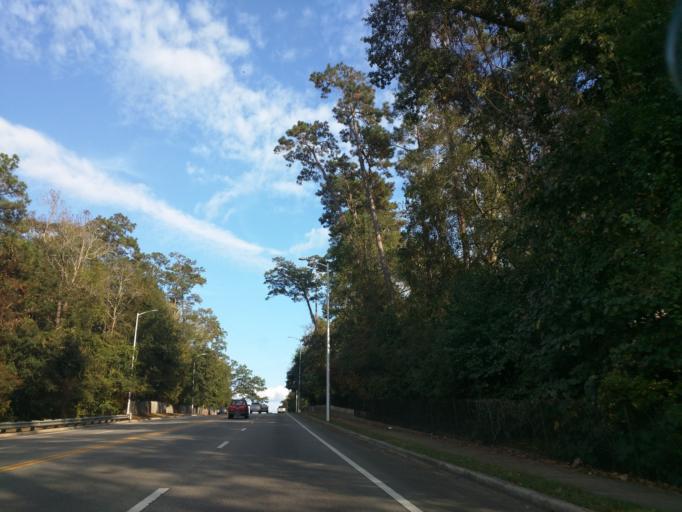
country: US
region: Florida
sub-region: Leon County
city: Tallahassee
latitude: 30.4418
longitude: -84.2391
